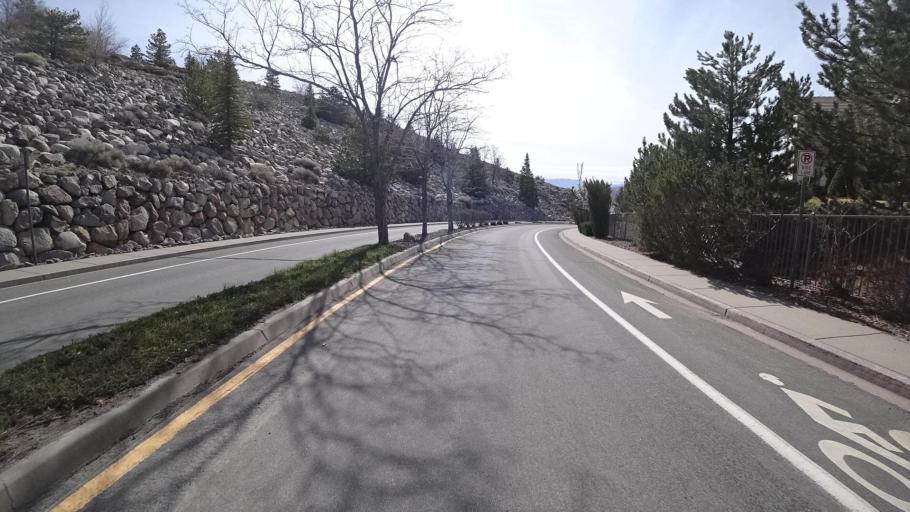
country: US
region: Nevada
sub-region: Washoe County
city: Mogul
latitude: 39.5380
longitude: -119.9011
